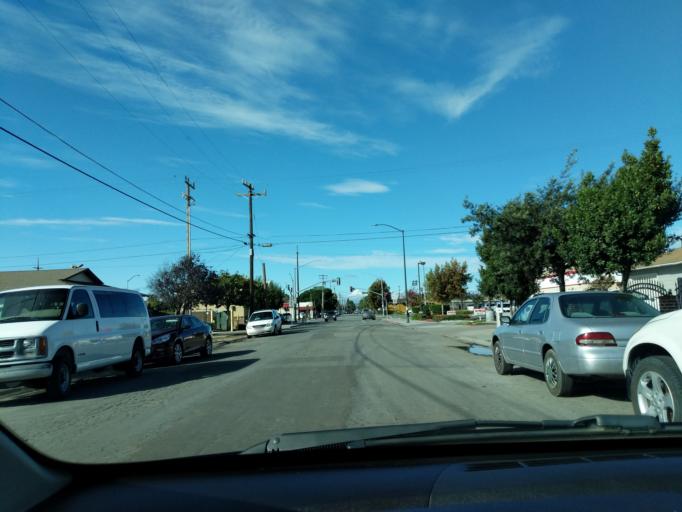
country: US
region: California
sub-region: Monterey County
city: Salinas
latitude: 36.6724
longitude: -121.6324
